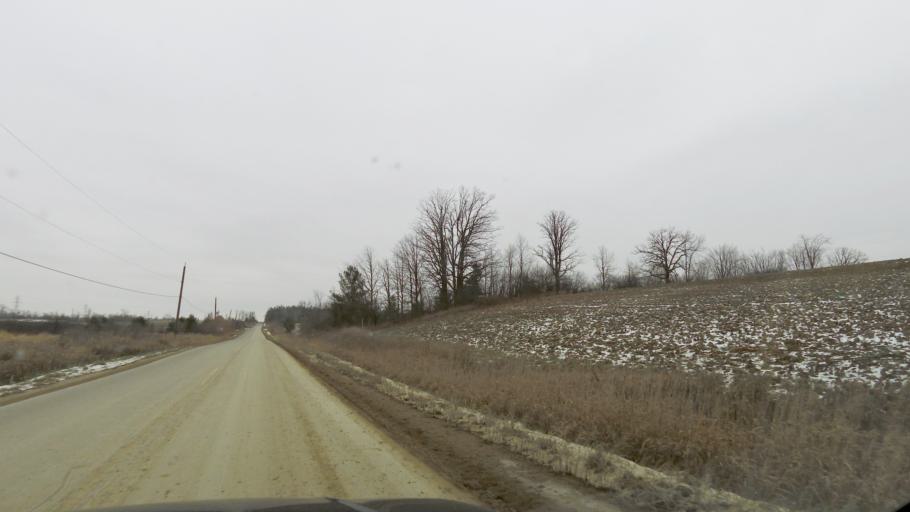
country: CA
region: Ontario
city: Vaughan
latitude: 43.8665
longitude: -79.6175
